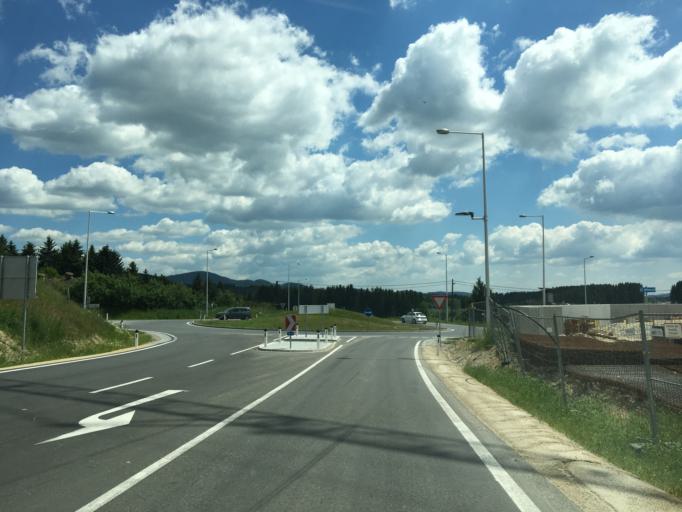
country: AT
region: Upper Austria
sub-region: Politischer Bezirk Freistadt
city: Freistadt
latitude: 48.4870
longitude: 14.4976
